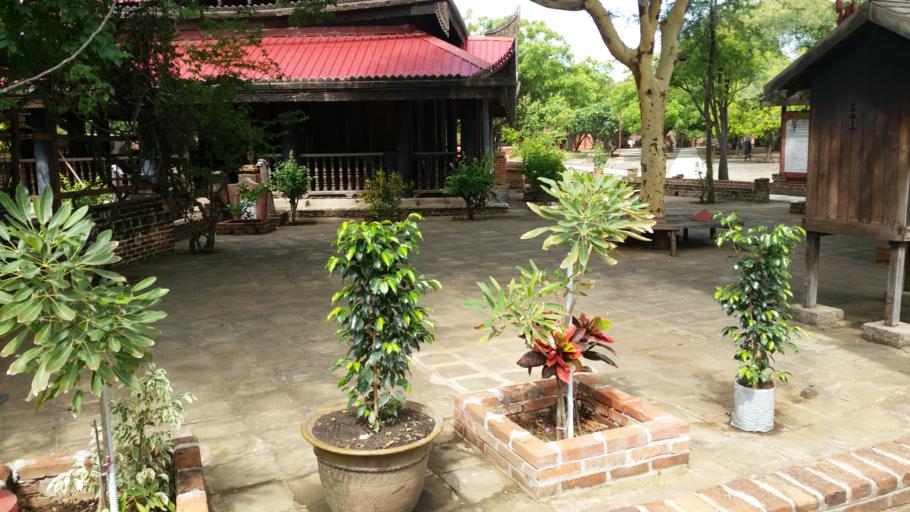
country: MM
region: Magway
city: Chauk
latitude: 21.1444
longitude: 94.8836
